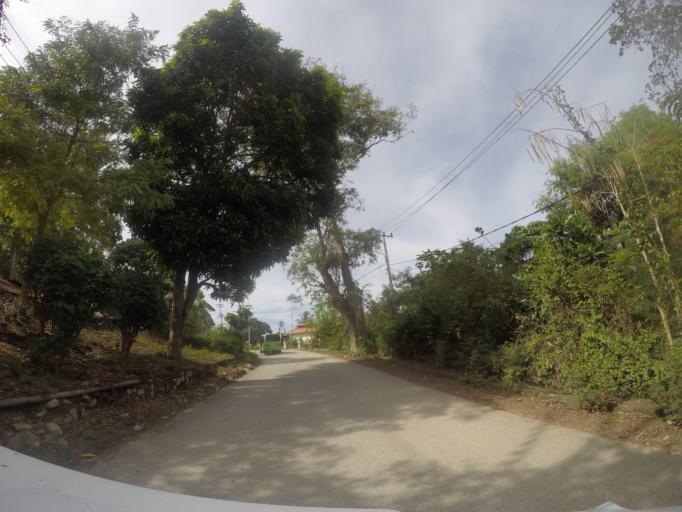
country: TL
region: Baucau
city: Baucau
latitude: -8.4824
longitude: 126.4570
